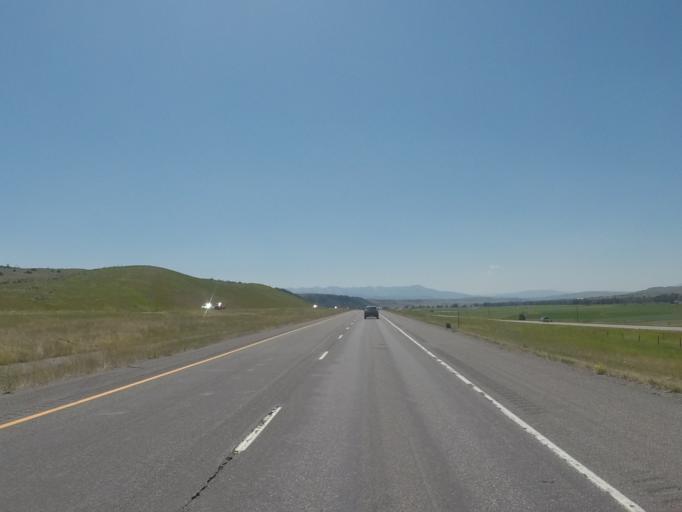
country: US
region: Montana
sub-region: Sweet Grass County
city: Big Timber
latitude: 45.7911
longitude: -110.0434
